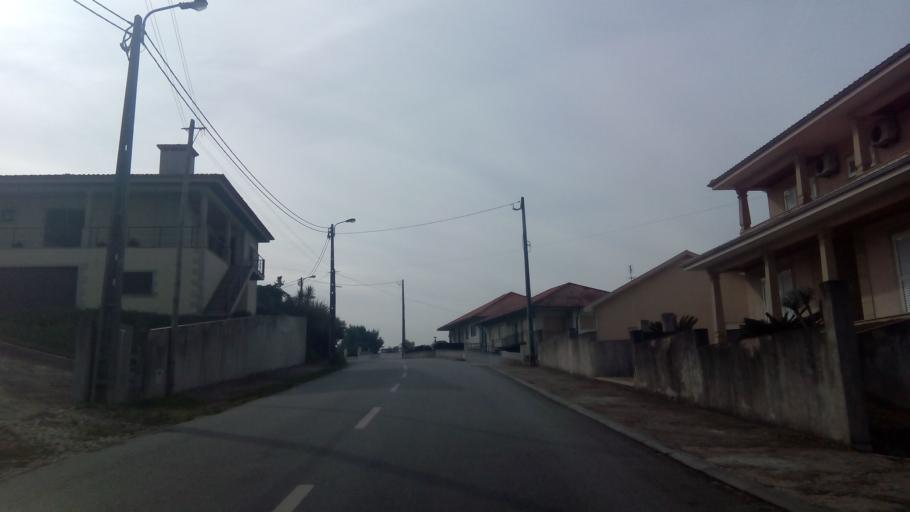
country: PT
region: Porto
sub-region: Paredes
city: Gandra
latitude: 41.1919
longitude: -8.4296
